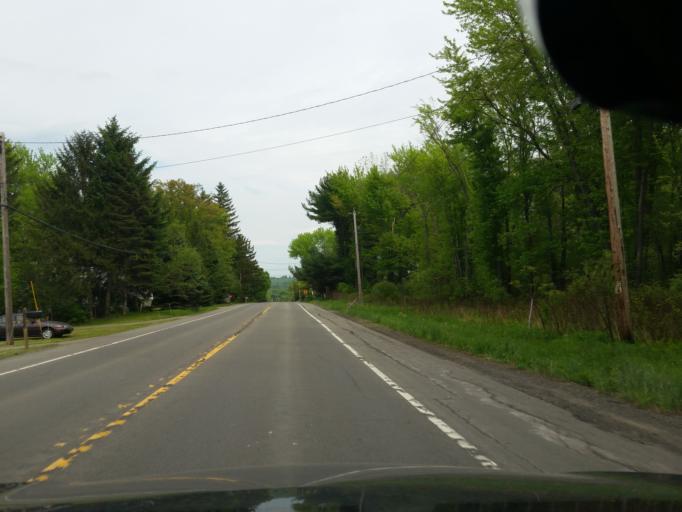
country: US
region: New York
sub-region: Chautauqua County
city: Lakewood
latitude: 42.1087
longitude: -79.3784
